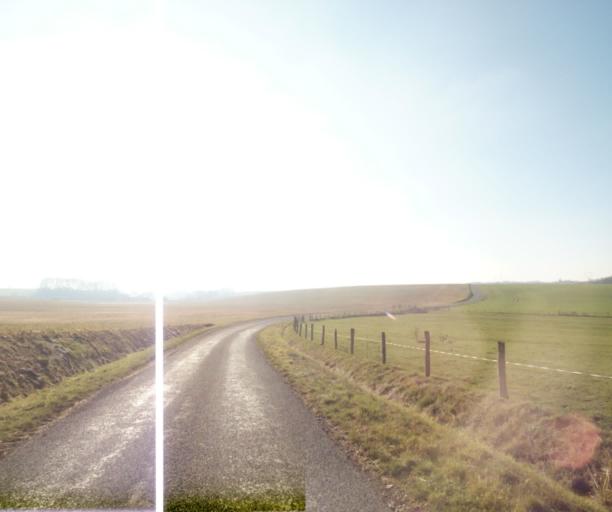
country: FR
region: Champagne-Ardenne
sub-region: Departement de la Haute-Marne
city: Wassy
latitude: 48.5217
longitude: 4.9903
